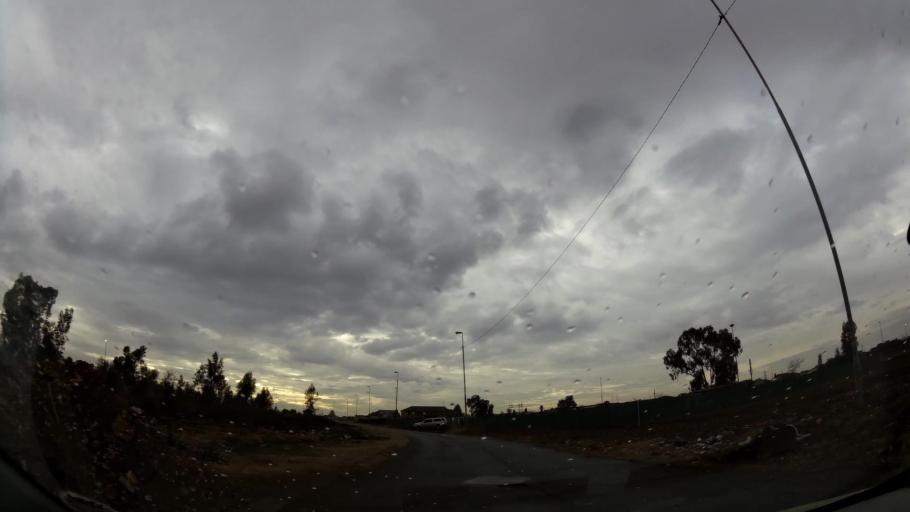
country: ZA
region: Gauteng
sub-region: Ekurhuleni Metropolitan Municipality
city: Germiston
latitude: -26.3377
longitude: 28.1953
